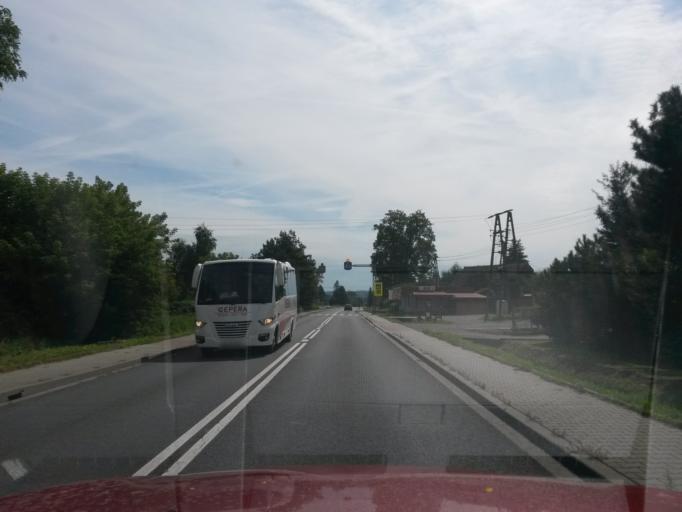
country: PL
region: Lesser Poland Voivodeship
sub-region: Powiat wielicki
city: Targowisko
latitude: 49.9806
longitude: 20.2904
